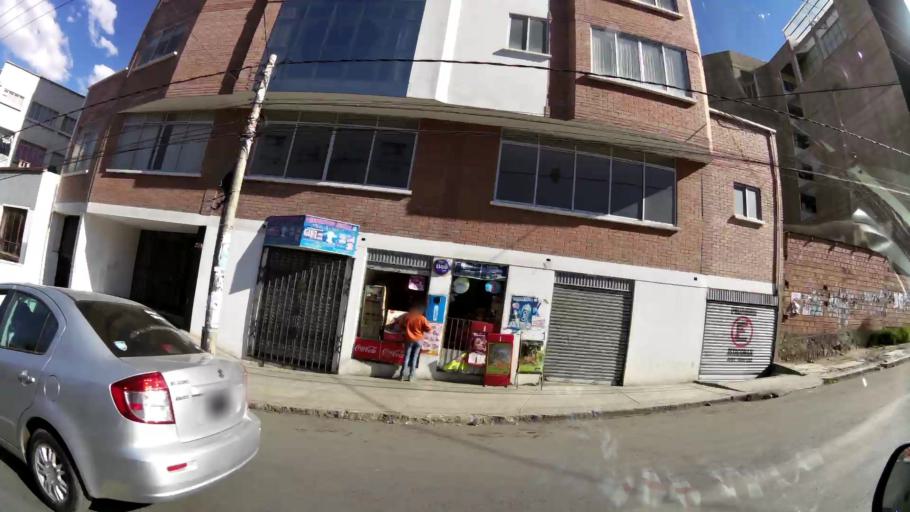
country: BO
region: La Paz
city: La Paz
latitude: -16.5155
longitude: -68.1351
